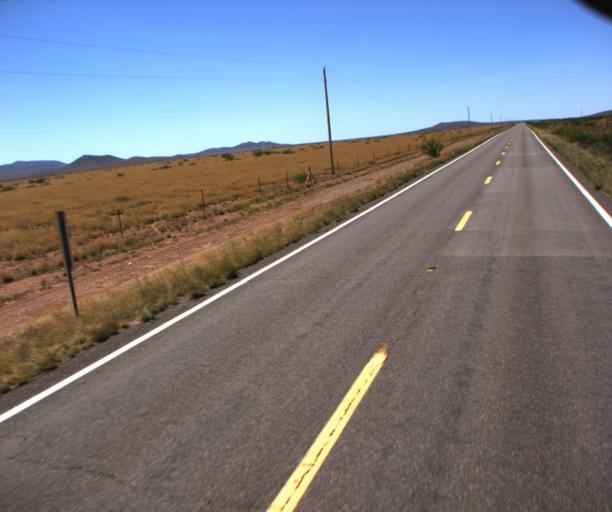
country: US
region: Arizona
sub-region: Cochise County
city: Douglas
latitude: 31.6691
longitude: -109.1477
